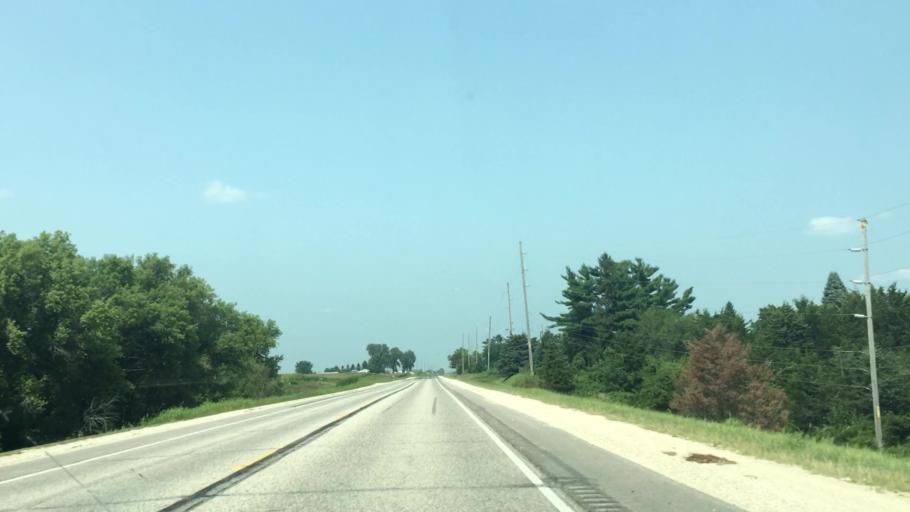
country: US
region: Iowa
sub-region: Fayette County
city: Fayette
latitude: 42.8759
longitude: -91.8105
